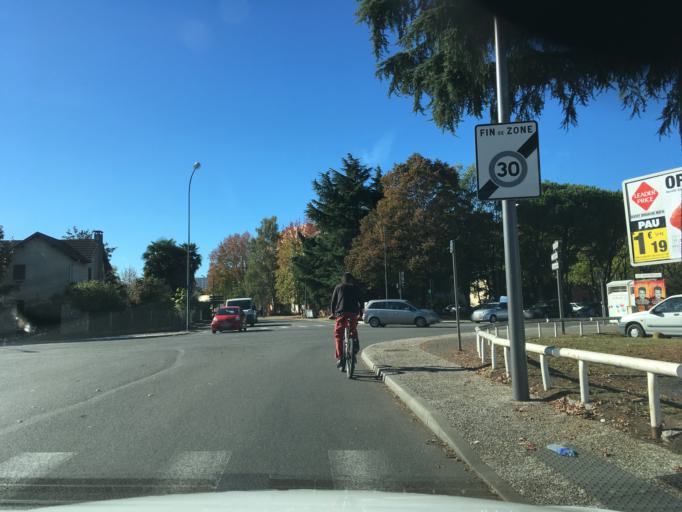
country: FR
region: Aquitaine
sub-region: Departement des Pyrenees-Atlantiques
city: Pau
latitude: 43.3112
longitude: -0.3515
